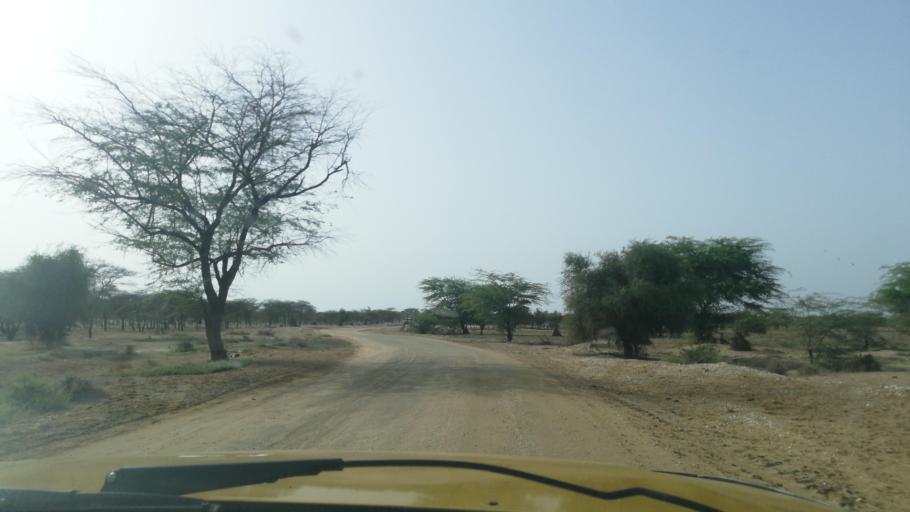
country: SN
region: Saint-Louis
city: Saint-Louis
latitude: 16.0593
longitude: -16.3328
